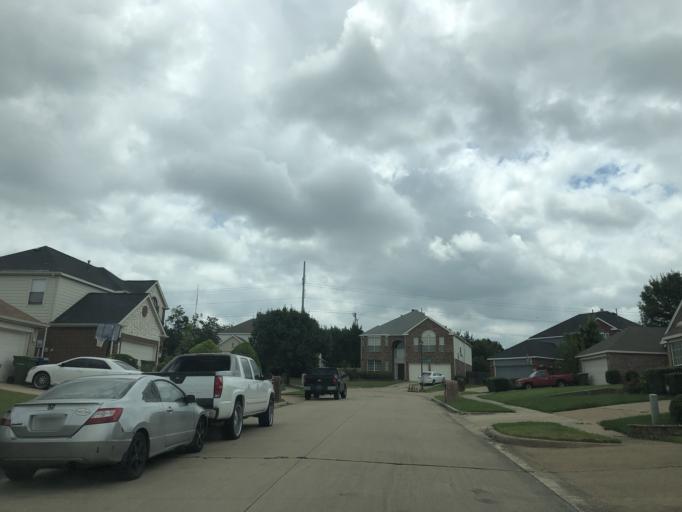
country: US
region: Texas
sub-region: Dallas County
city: Sunnyvale
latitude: 32.8413
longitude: -96.5709
